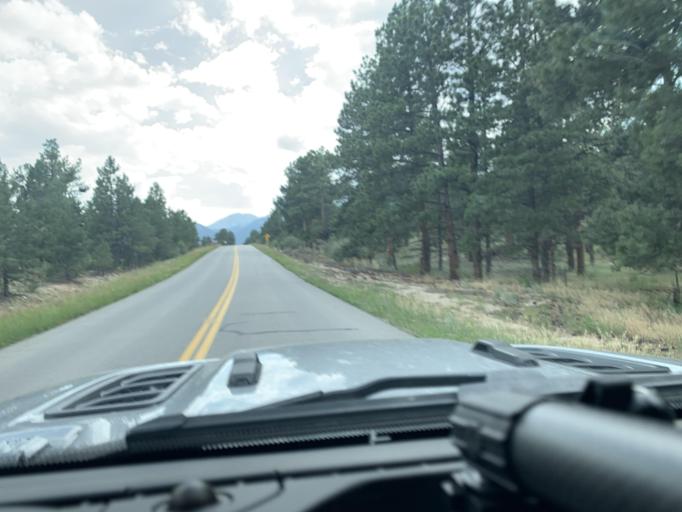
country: US
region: Colorado
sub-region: Chaffee County
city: Buena Vista
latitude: 38.7450
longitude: -106.1609
